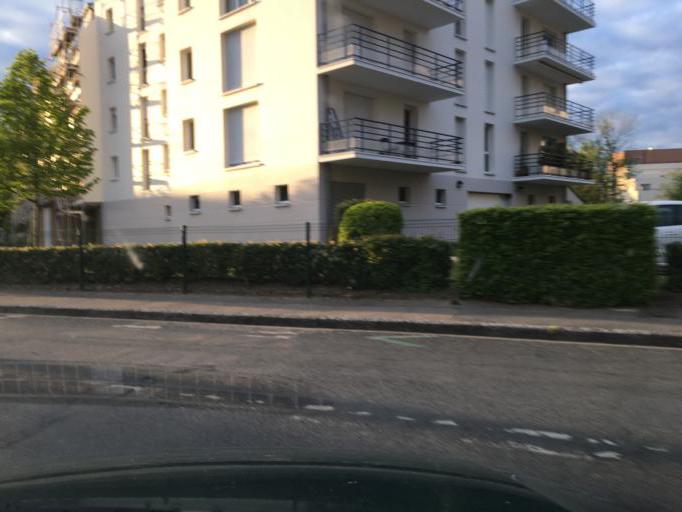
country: FR
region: Centre
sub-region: Departement du Loiret
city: Saint-Jean-le-Blanc
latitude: 47.8831
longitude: 1.9080
